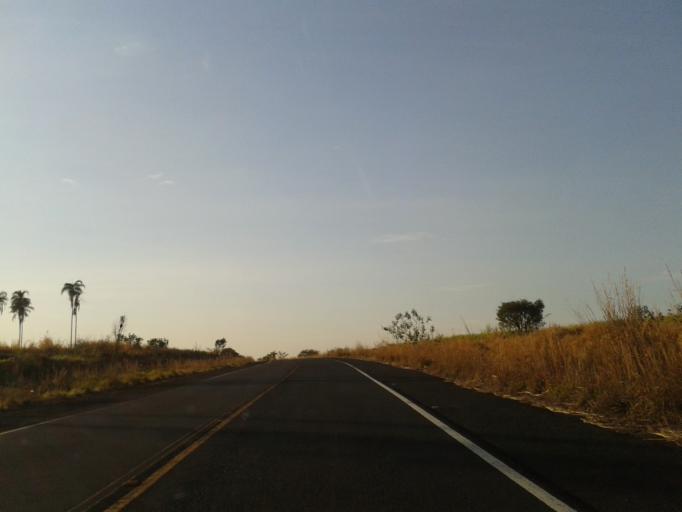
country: BR
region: Minas Gerais
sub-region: Santa Vitoria
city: Santa Vitoria
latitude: -19.1176
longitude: -50.3085
